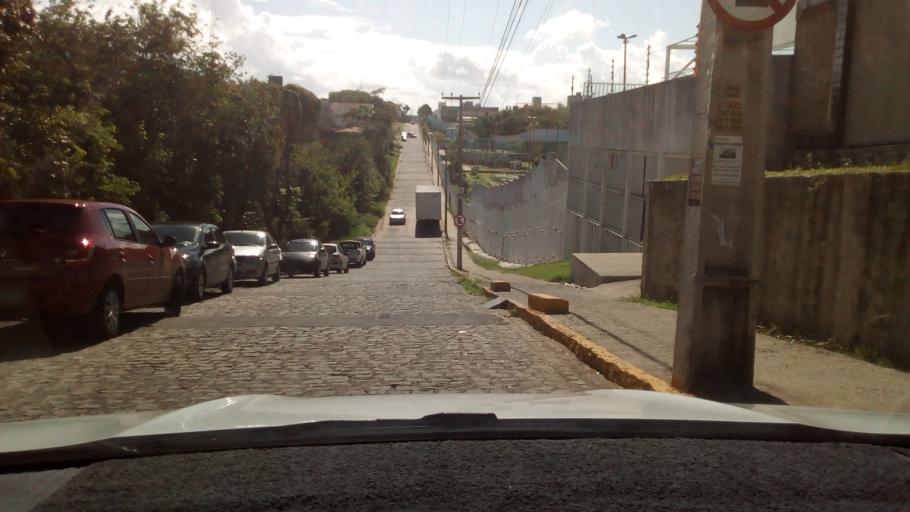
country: BR
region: Paraiba
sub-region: Joao Pessoa
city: Joao Pessoa
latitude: -7.1569
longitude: -34.8154
